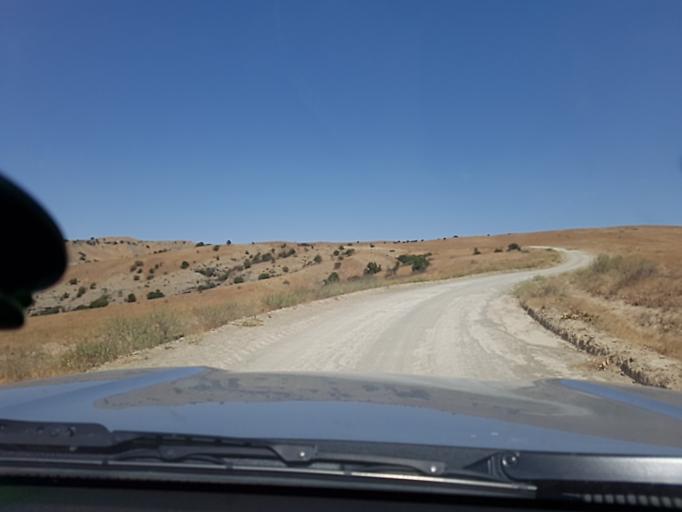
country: TM
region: Balkan
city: Magtymguly
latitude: 38.3463
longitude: 56.8264
